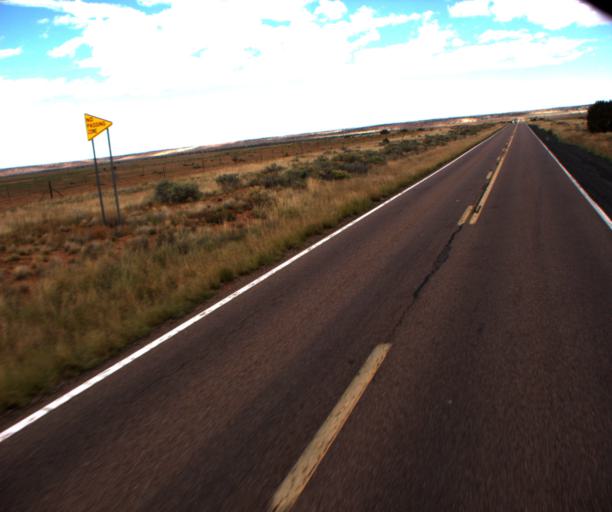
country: US
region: Arizona
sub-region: Navajo County
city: Heber-Overgaard
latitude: 34.6061
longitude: -110.3830
